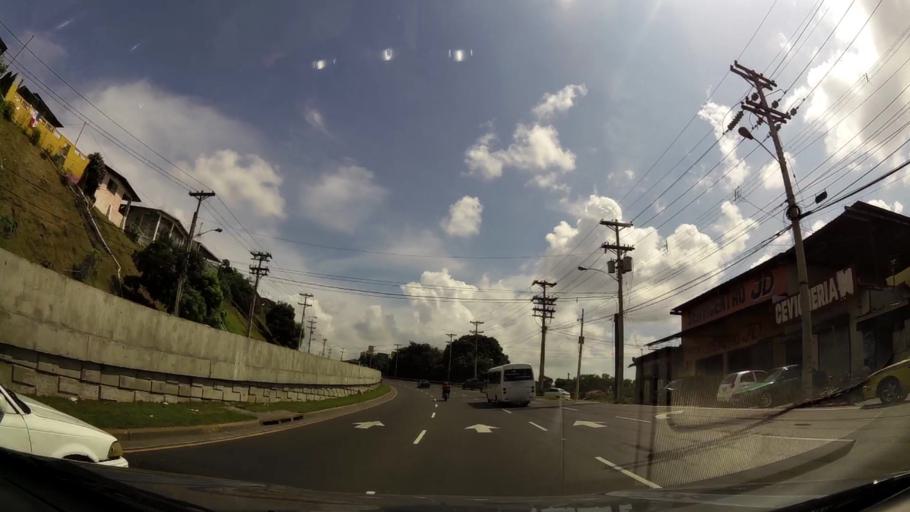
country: PA
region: Panama
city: San Miguelito
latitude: 9.0288
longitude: -79.4948
